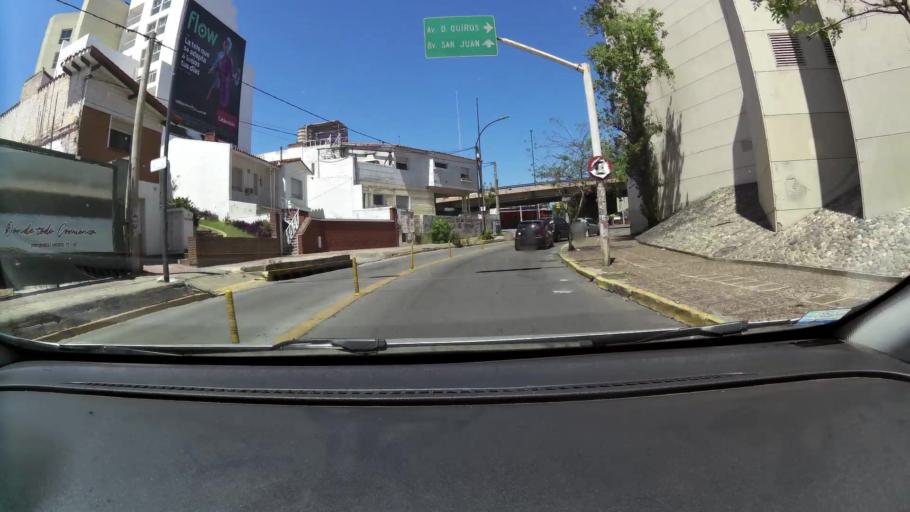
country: AR
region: Cordoba
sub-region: Departamento de Capital
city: Cordoba
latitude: -31.4136
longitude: -64.2019
